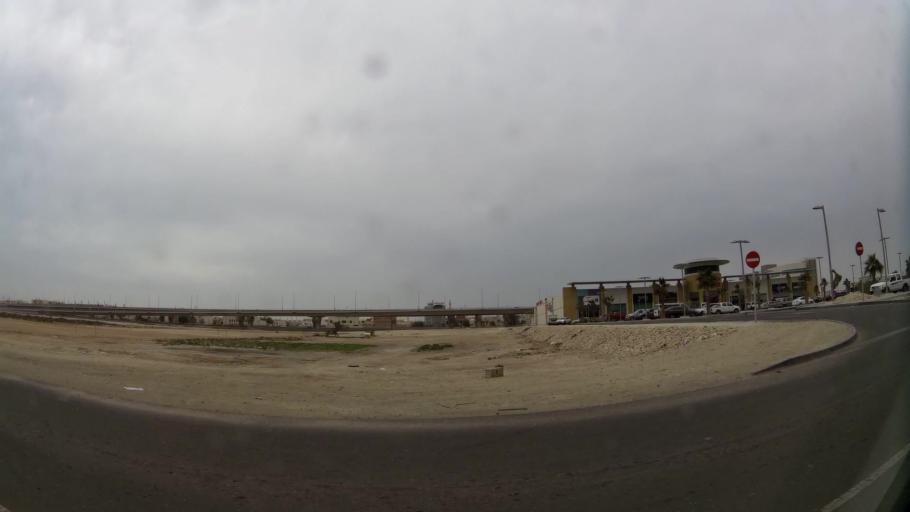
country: BH
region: Northern
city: Madinat `Isa
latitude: 26.1707
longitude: 50.5390
